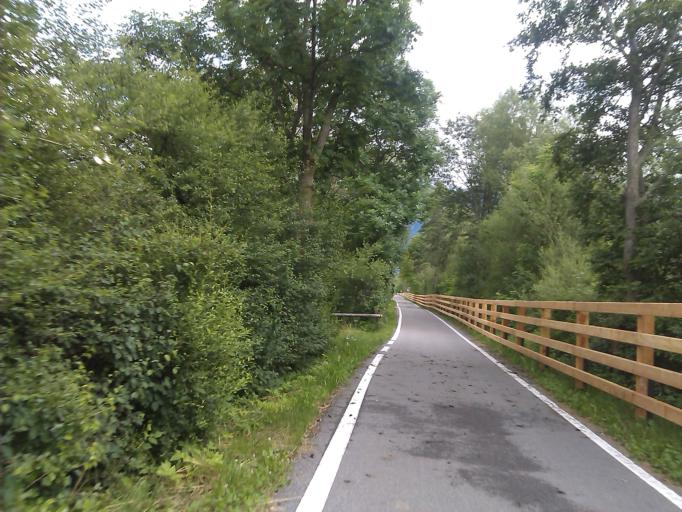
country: IT
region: Trentino-Alto Adige
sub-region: Bolzano
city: Glorenza
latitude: 46.6637
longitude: 10.5629
